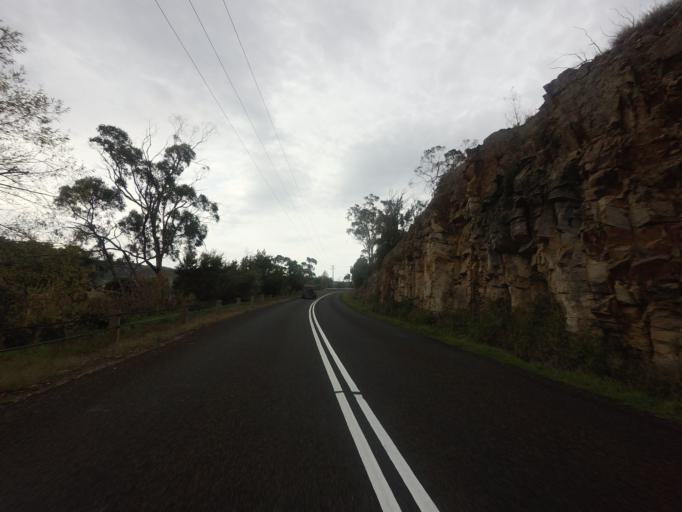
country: AU
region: Tasmania
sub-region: Brighton
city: Bridgewater
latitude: -42.6756
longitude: 147.1605
